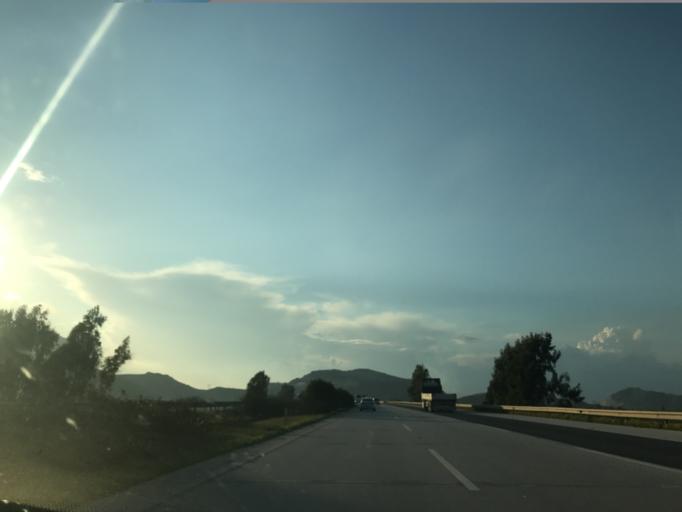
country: TR
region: Adana
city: Ceyhan
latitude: 36.9858
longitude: 35.7668
